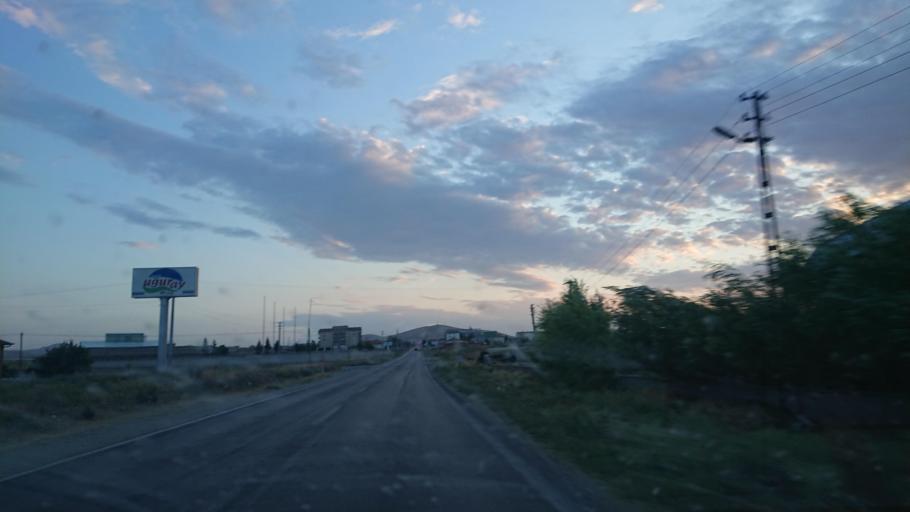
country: TR
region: Aksaray
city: Balci
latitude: 38.7576
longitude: 34.0791
